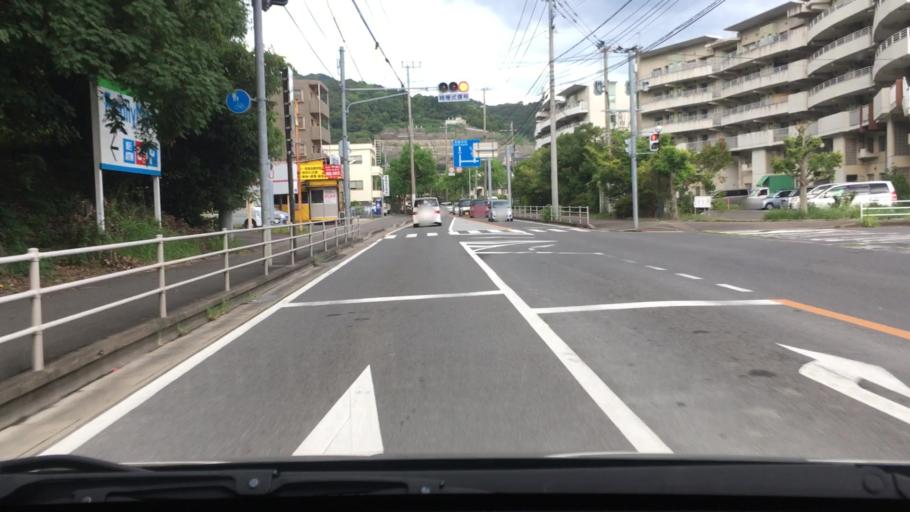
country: JP
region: Nagasaki
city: Togitsu
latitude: 32.8277
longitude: 129.7781
